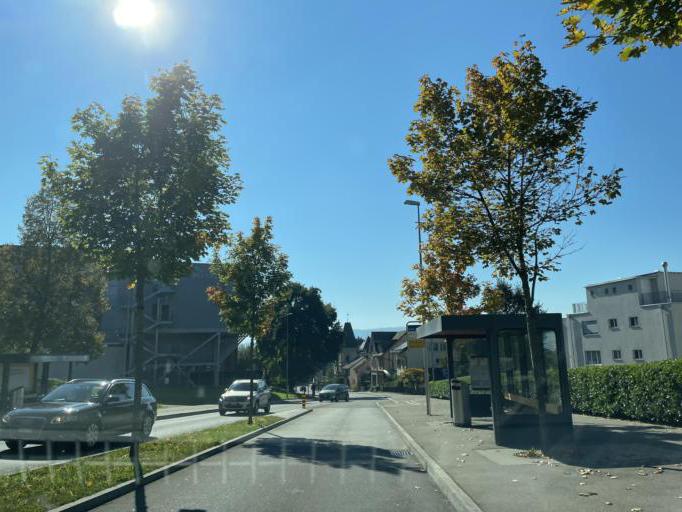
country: CH
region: Zurich
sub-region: Bezirk Uster
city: Uster
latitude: 47.3541
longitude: 8.7236
